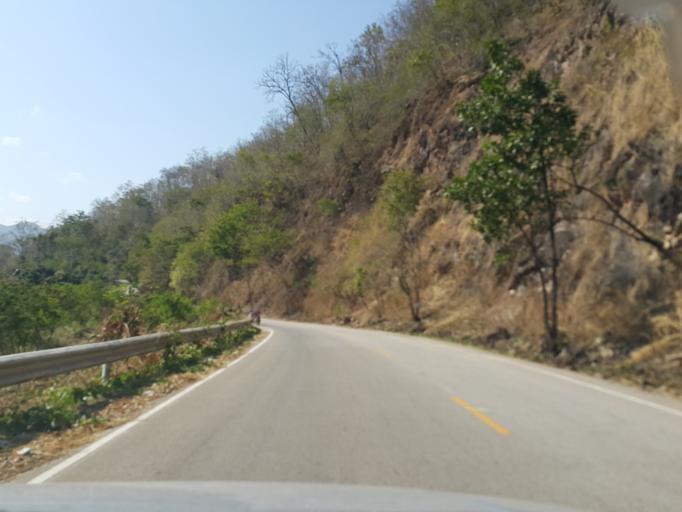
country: TH
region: Chiang Mai
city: Mae Wang
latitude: 18.6172
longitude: 98.7549
